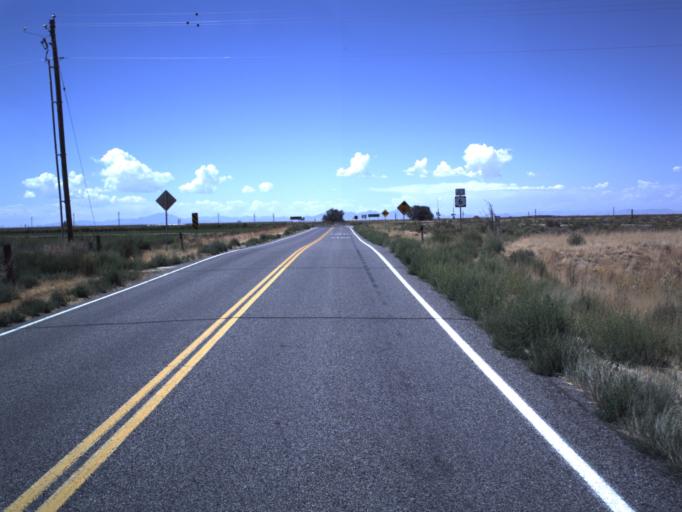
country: US
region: Utah
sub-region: Millard County
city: Delta
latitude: 39.5245
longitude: -112.3682
